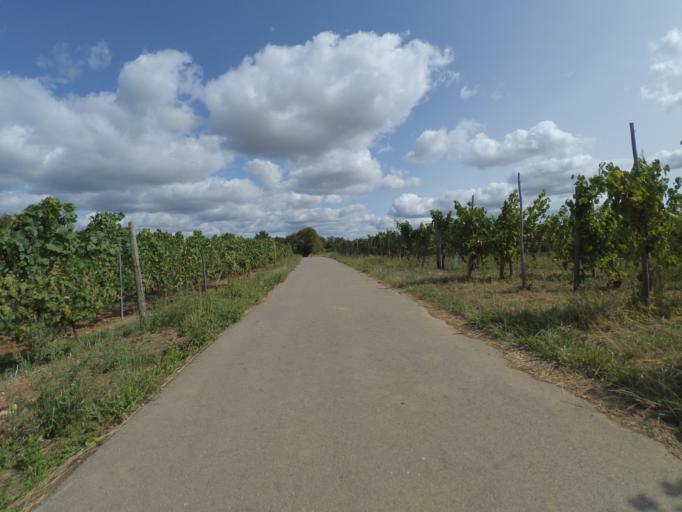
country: LU
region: Grevenmacher
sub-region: Canton de Remich
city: Lenningen
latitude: 49.6016
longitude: 6.3796
